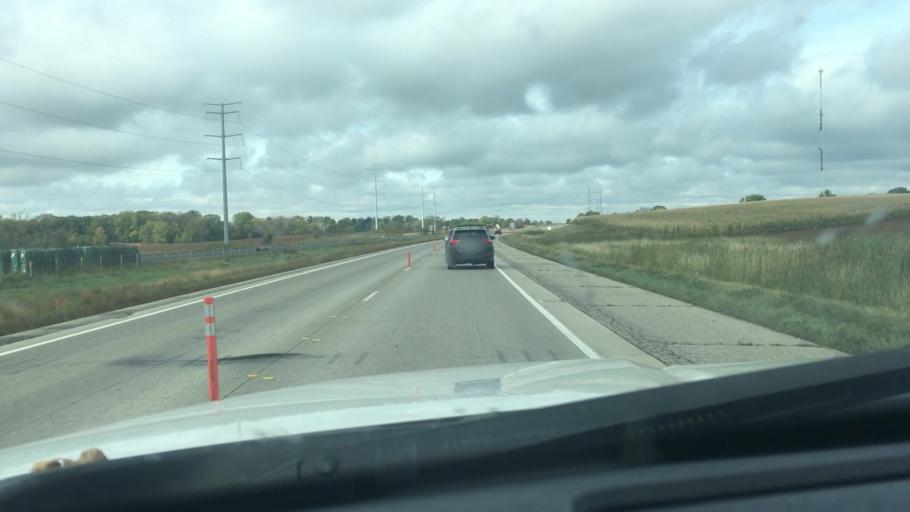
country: US
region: Minnesota
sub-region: Douglas County
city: Alexandria
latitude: 45.9147
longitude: -95.5491
